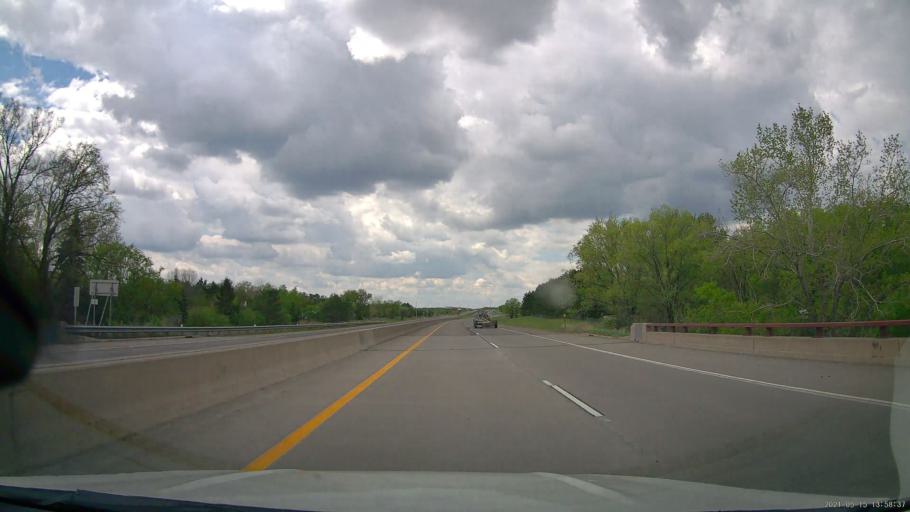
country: US
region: Minnesota
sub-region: Morrison County
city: Little Falls
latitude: 46.0000
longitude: -94.3691
